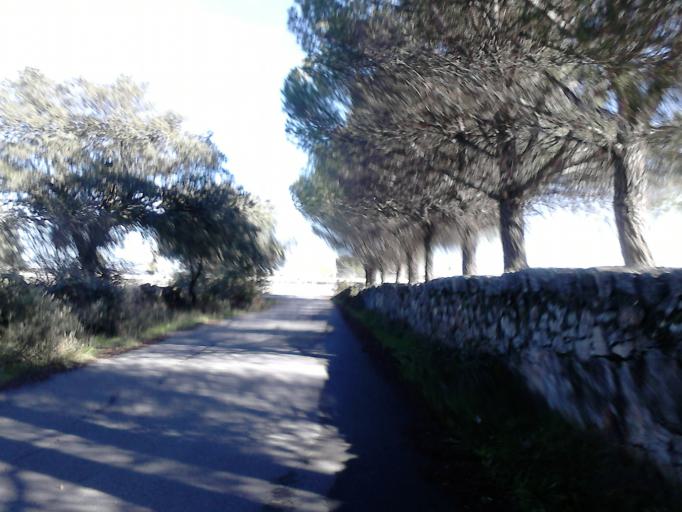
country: ES
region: Madrid
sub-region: Provincia de Madrid
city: Galapagar
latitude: 40.5741
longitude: -3.9873
